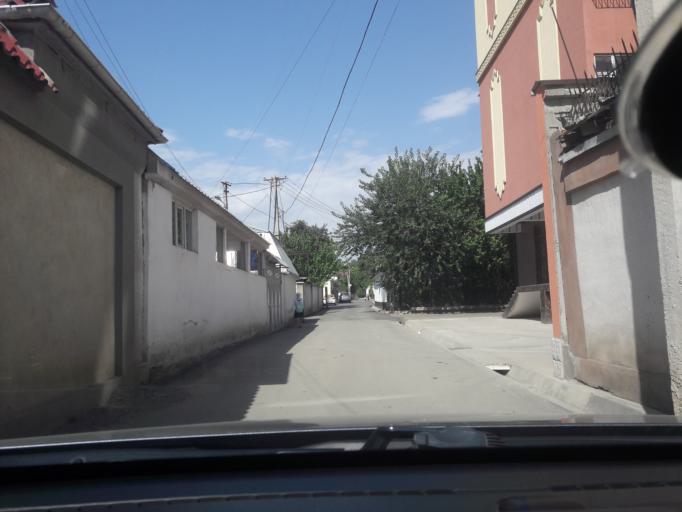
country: TJ
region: Dushanbe
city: Dushanbe
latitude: 38.5753
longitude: 68.7969
